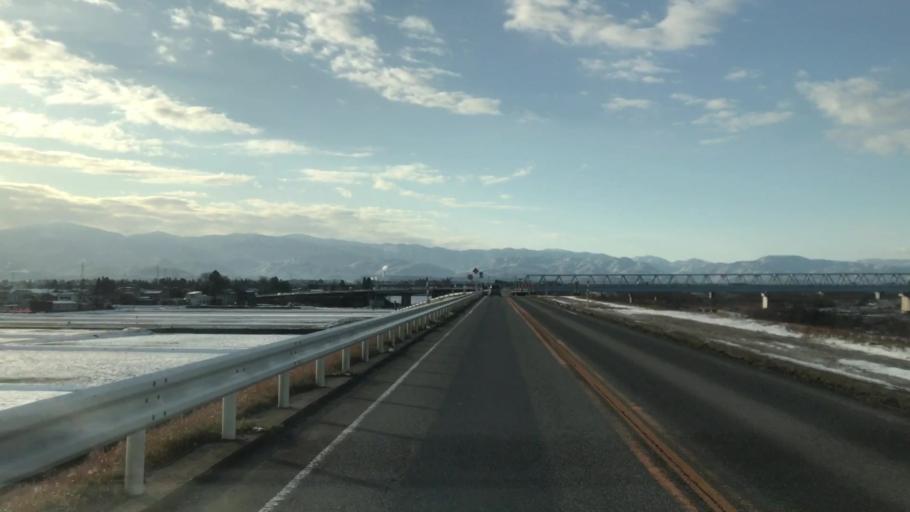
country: JP
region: Toyama
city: Toyama-shi
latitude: 36.6762
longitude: 137.2854
